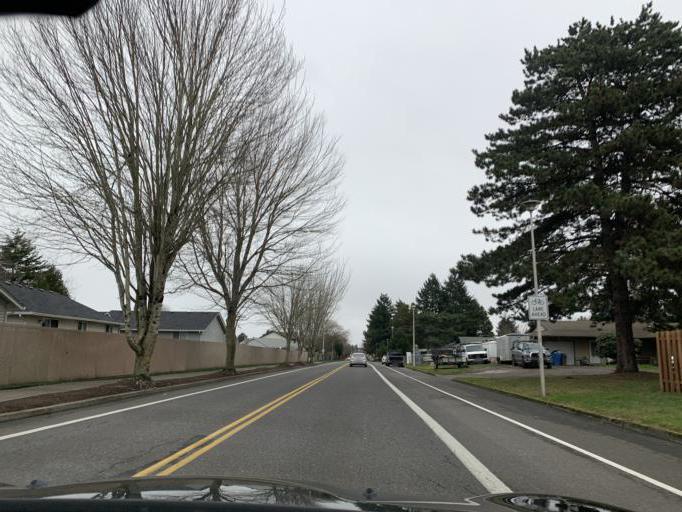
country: US
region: Washington
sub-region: Clark County
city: Mill Plain
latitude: 45.6212
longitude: -122.5127
